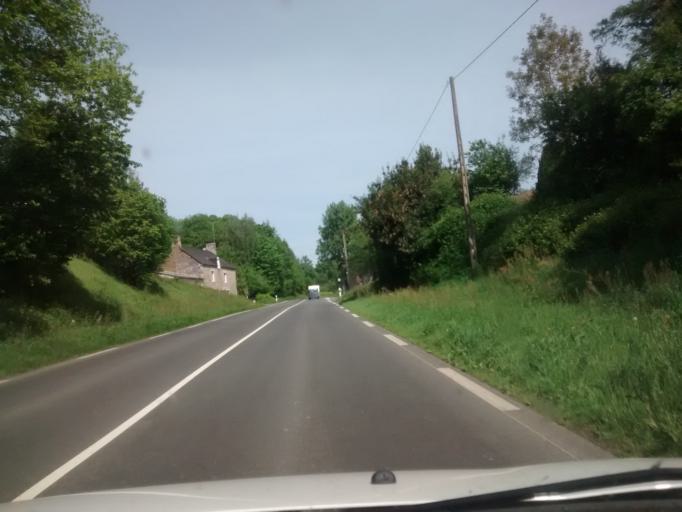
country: FR
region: Brittany
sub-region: Departement d'Ille-et-Vilaine
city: Antrain
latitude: 48.4634
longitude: -1.5072
